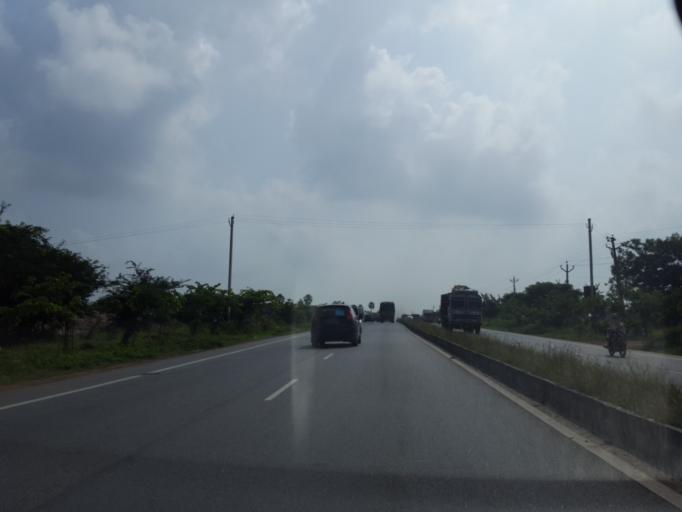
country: IN
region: Telangana
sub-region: Rangareddi
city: Ghatkesar
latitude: 17.2939
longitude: 78.7453
